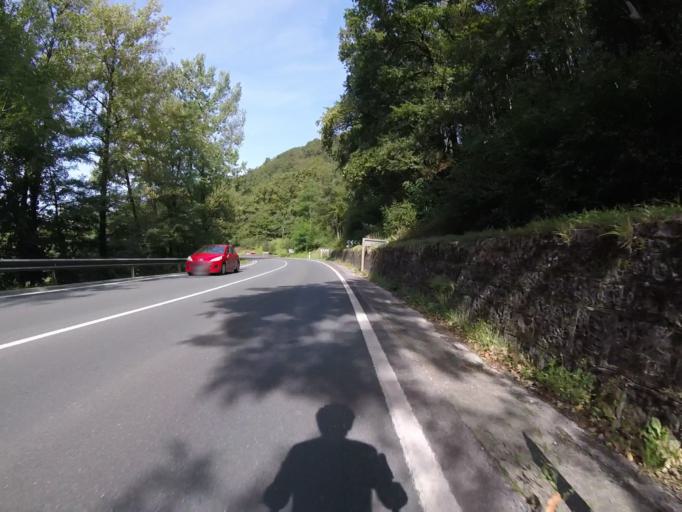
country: ES
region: Navarre
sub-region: Provincia de Navarra
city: Doneztebe
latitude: 43.1425
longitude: -1.5817
